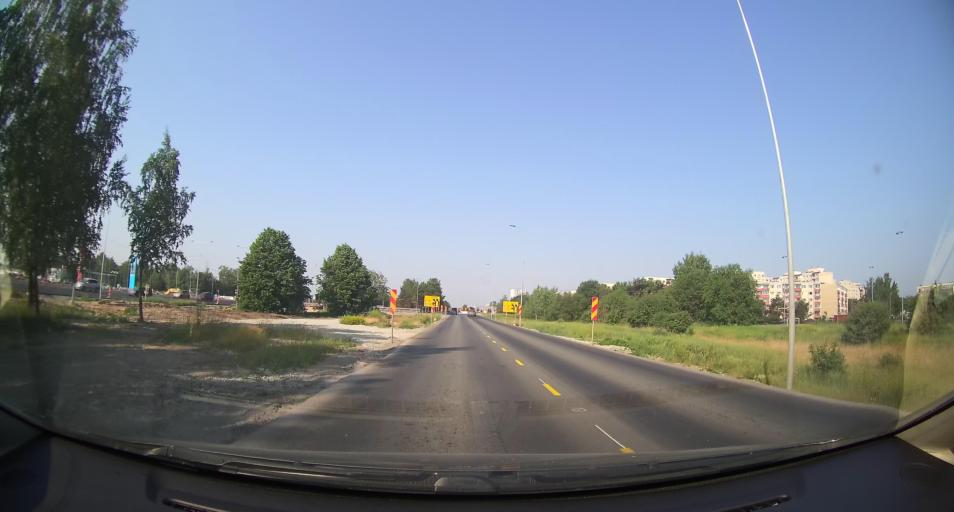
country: EE
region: Harju
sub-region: Tallinna linn
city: Kose
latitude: 59.4431
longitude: 24.9004
